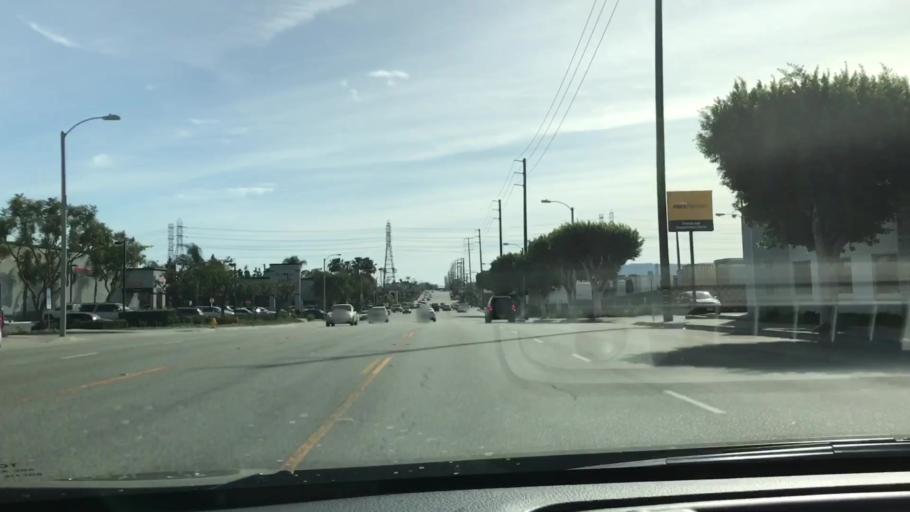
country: US
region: California
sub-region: Los Angeles County
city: Gardena
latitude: 33.8751
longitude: -118.3092
